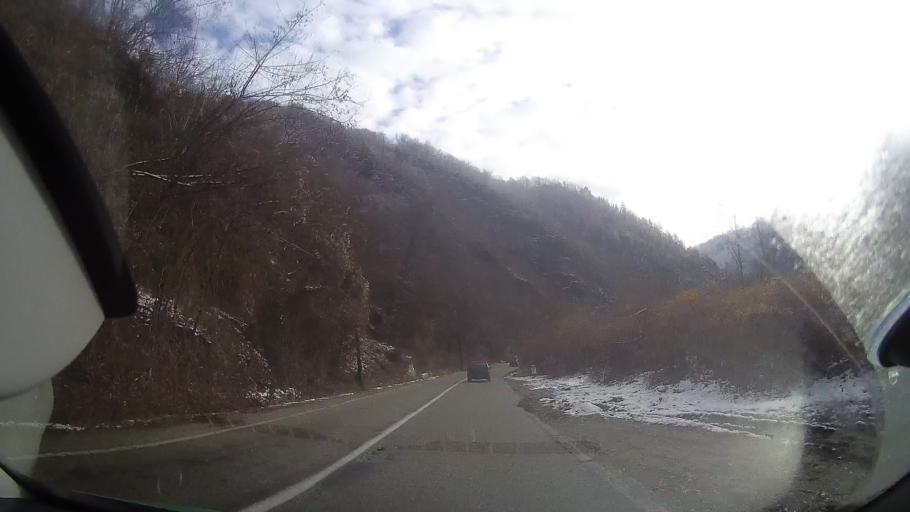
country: RO
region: Alba
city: Salciua de Sus
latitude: 46.4059
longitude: 23.3618
